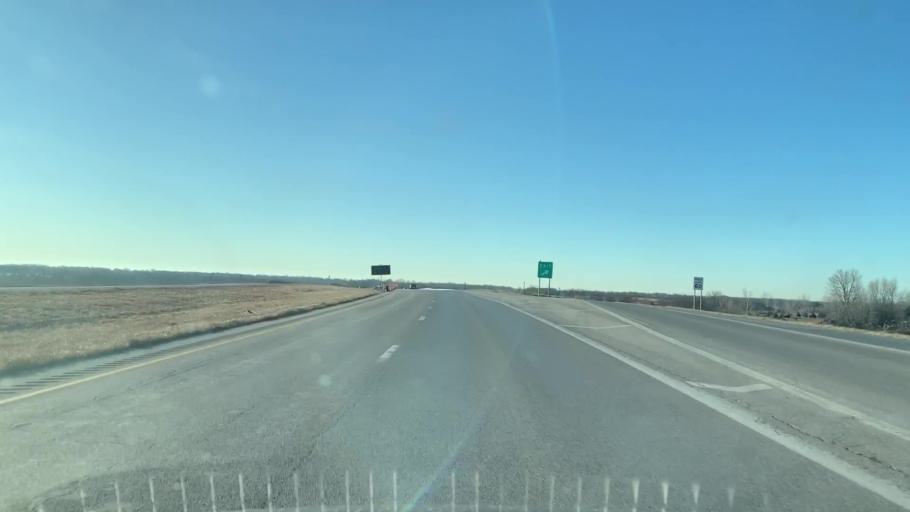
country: US
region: Kansas
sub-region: Bourbon County
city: Fort Scott
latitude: 37.7703
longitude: -94.7061
